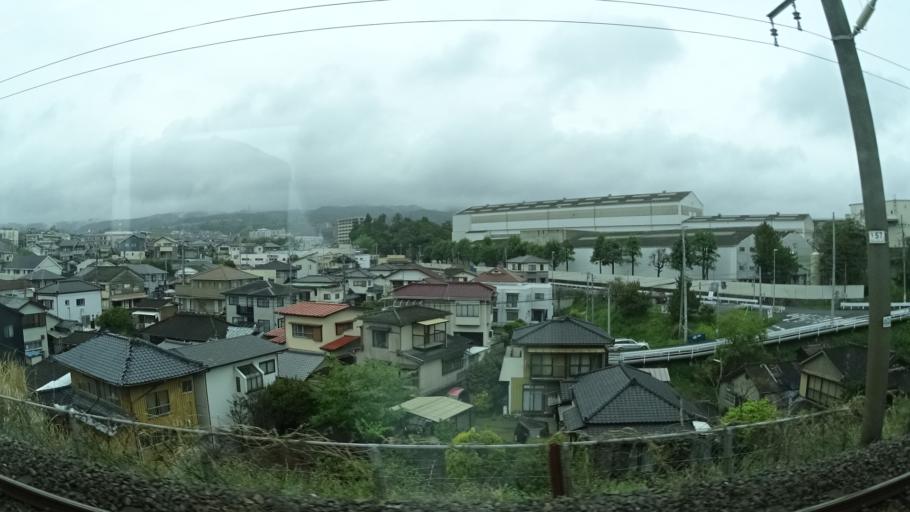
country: JP
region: Ibaraki
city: Hitachi
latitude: 36.5795
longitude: 140.6555
